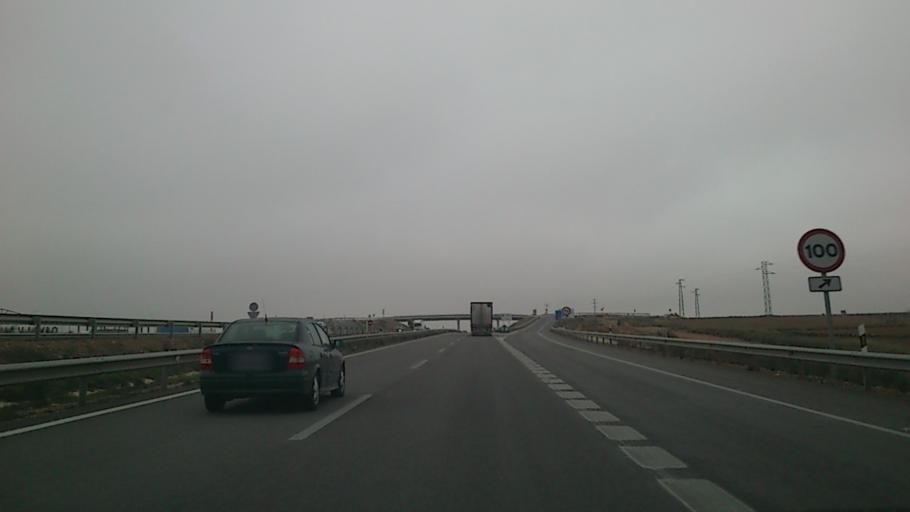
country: ES
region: Aragon
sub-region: Provincia de Zaragoza
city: Lucena de Jalon
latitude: 41.5358
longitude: -1.2463
